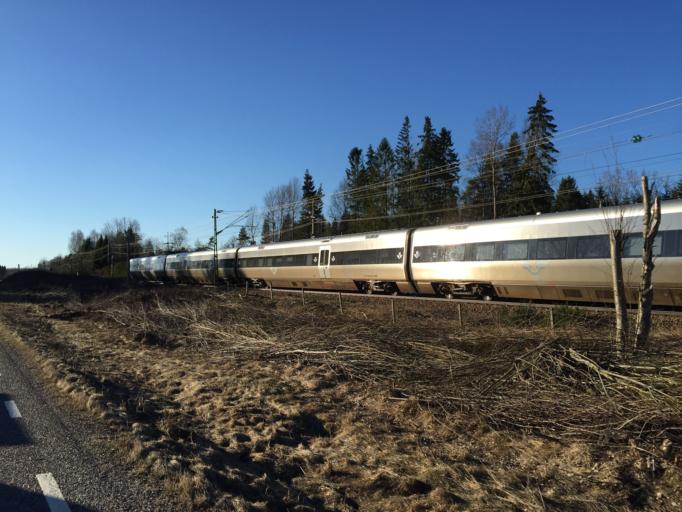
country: SE
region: Soedermanland
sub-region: Vingakers Kommun
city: Vingaker
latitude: 59.0468
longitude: 15.7762
